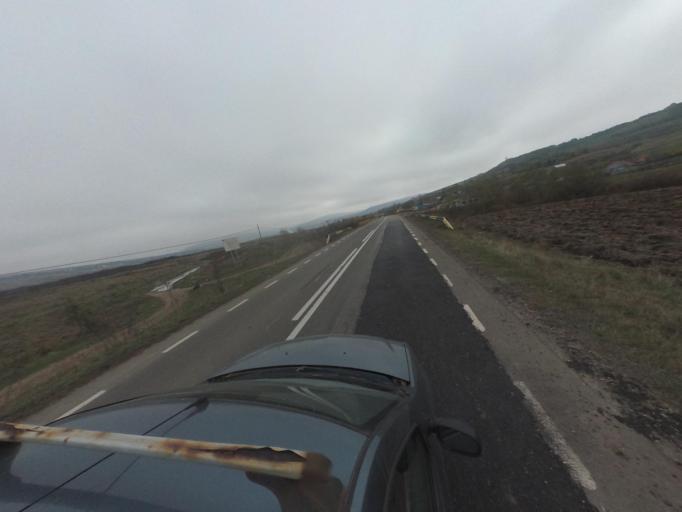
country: RO
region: Vaslui
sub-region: Comuna Bacesti
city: Bacesti
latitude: 46.8385
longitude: 27.2267
